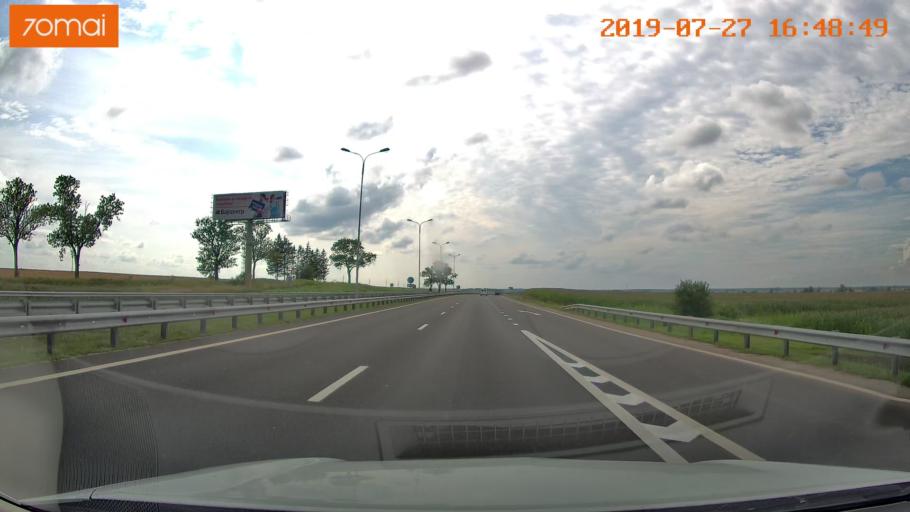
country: RU
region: Kaliningrad
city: Gvardeysk
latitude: 54.6706
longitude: 20.9570
